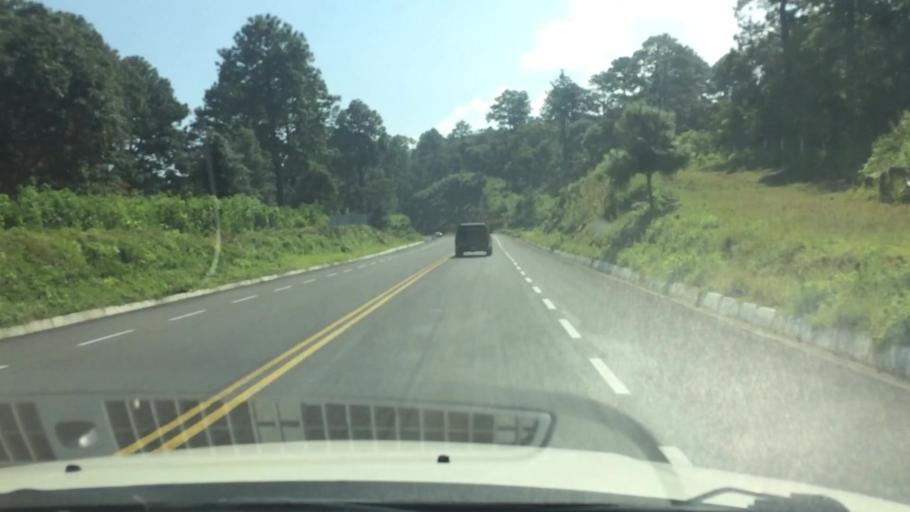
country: MX
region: Mexico
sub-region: Amanalco
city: Polvillos (San Bartolo Quinta Seccion)
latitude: 19.2198
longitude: -100.0918
